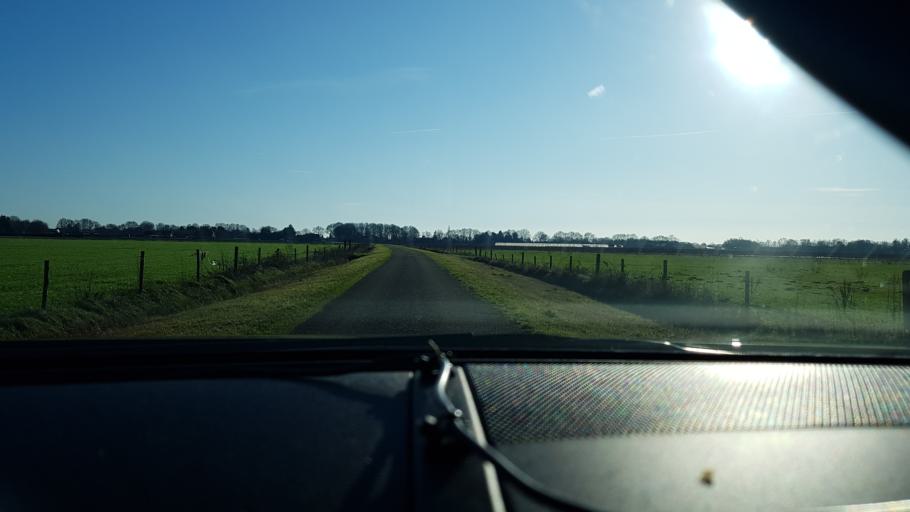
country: NL
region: Limburg
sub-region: Gemeente Leudal
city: Haelen
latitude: 51.2776
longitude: 5.9854
